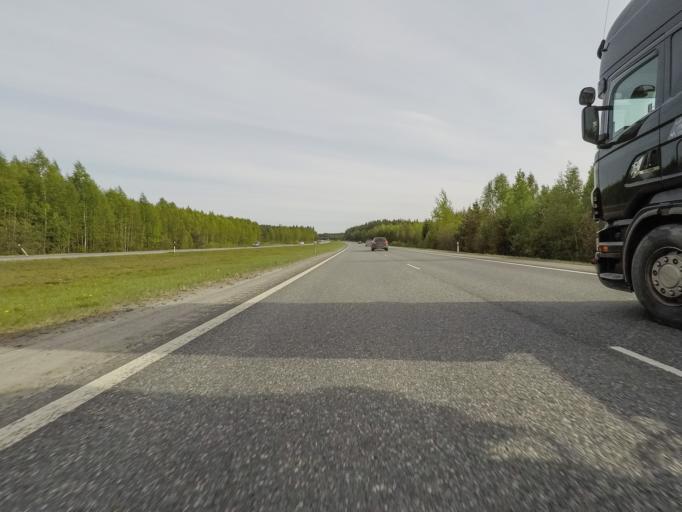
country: FI
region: Haeme
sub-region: Haemeenlinna
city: Haemeenlinna
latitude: 60.9319
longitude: 24.5181
